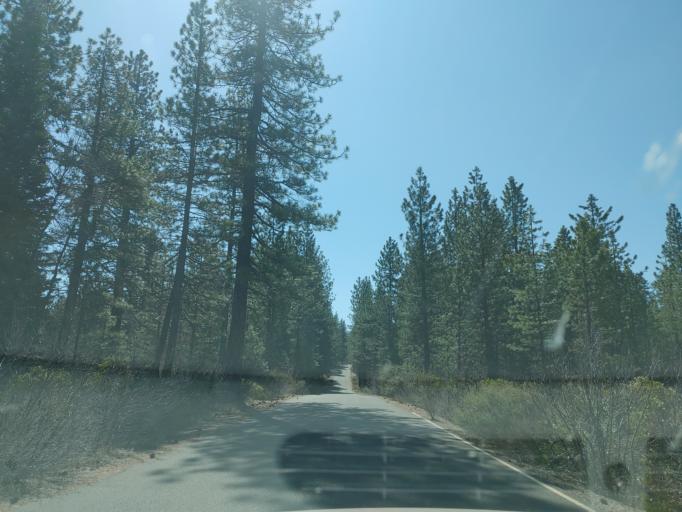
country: US
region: California
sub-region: Siskiyou County
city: McCloud
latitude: 41.2440
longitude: -122.0076
